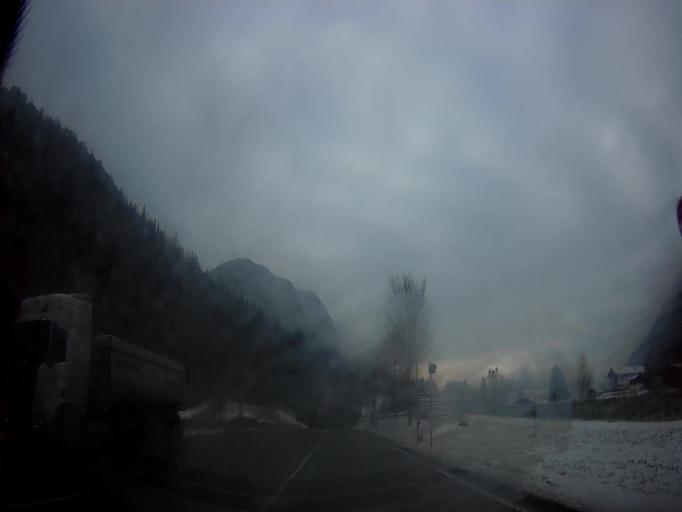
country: DE
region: Bavaria
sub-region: Upper Bavaria
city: Schneizlreuth
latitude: 47.6739
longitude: 12.7647
